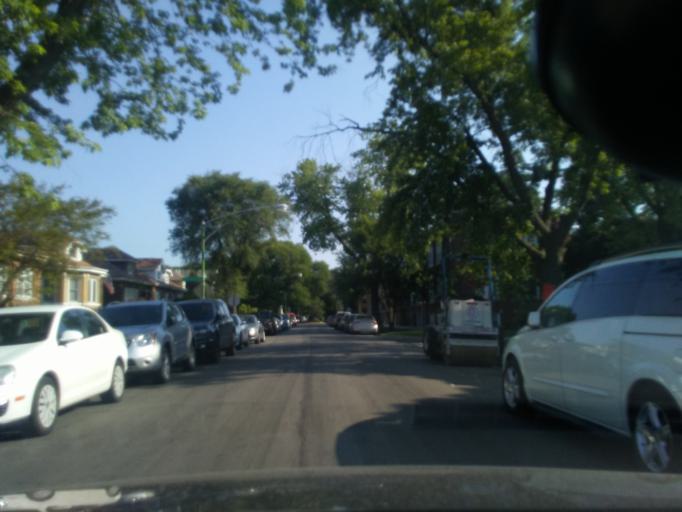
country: US
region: Illinois
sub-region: Cook County
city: Elmwood Park
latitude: 41.9338
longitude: -87.7614
